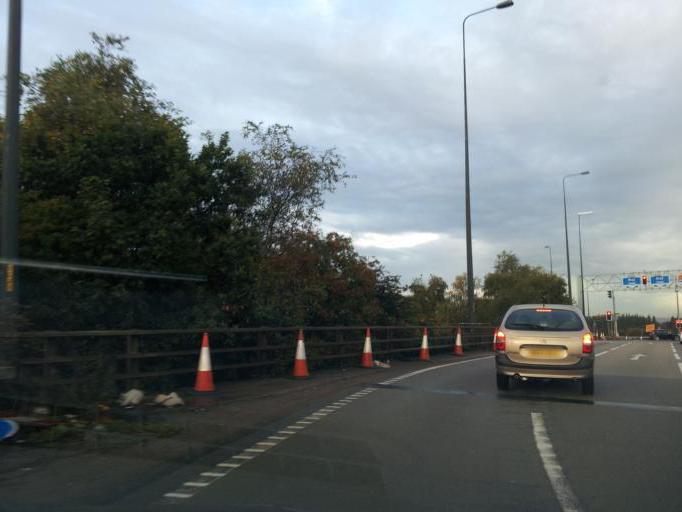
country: GB
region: England
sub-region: Borough of Bury
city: Prestwich
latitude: 53.5503
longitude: -2.2620
